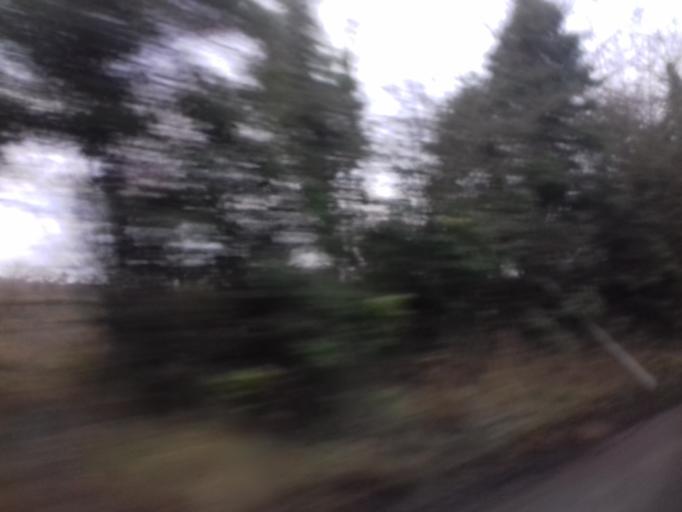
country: IE
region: Leinster
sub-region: An Mhi
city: Slane
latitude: 53.6858
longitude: -6.4857
